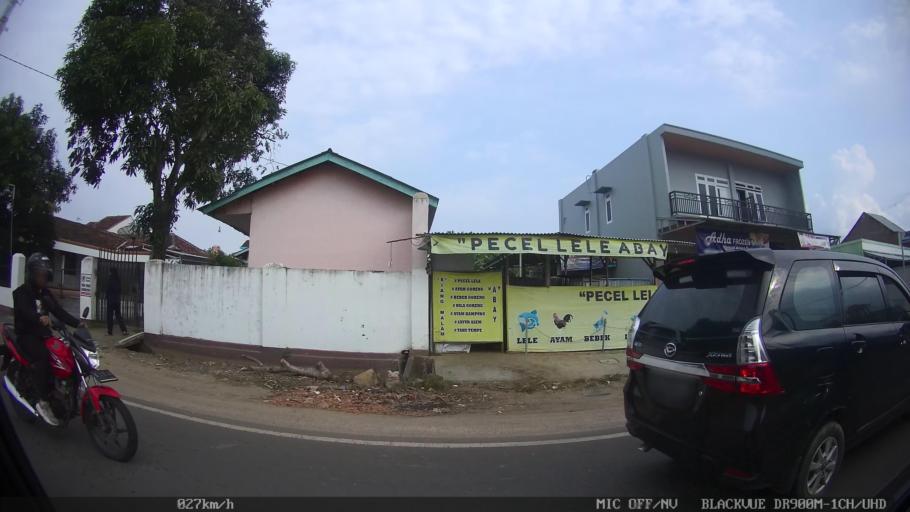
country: ID
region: Lampung
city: Kedaton
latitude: -5.3629
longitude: 105.2232
